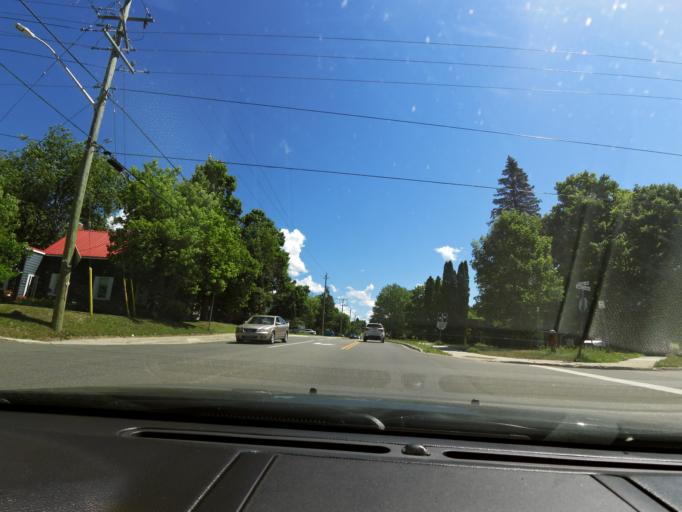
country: CA
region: Ontario
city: Bracebridge
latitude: 45.0425
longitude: -79.3074
